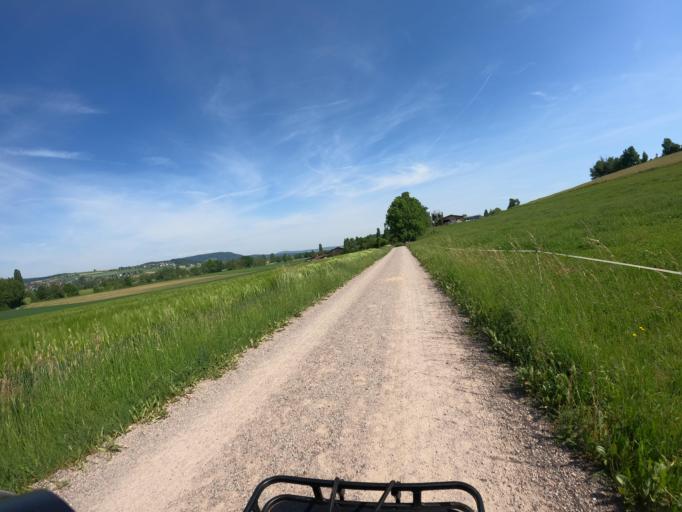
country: CH
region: Zurich
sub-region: Bezirk Dielsdorf
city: Niederglatt
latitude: 47.4922
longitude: 8.4903
